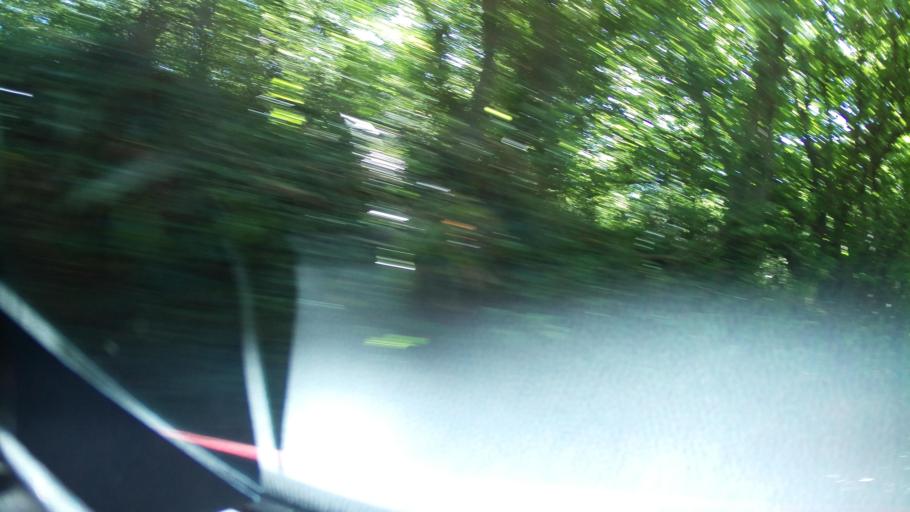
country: GB
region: England
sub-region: Devon
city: Ipplepen
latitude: 50.4992
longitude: -3.6167
